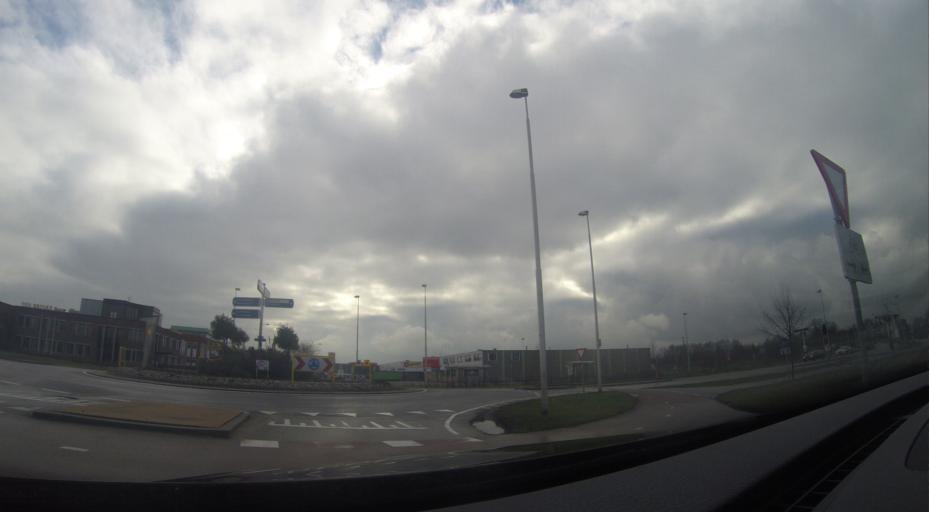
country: NL
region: Gelderland
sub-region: Gemeente Doetinchem
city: Doetinchem
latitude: 51.9524
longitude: 6.2890
